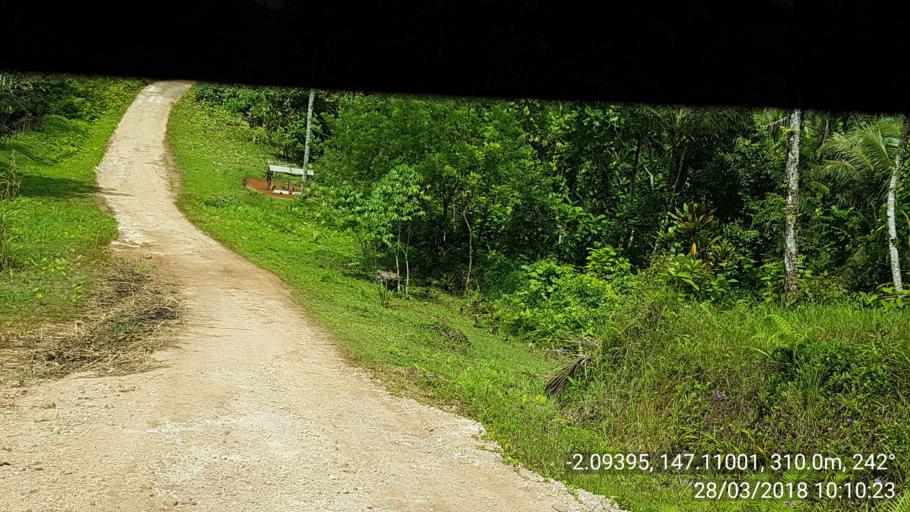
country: PG
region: Manus
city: Lorengau
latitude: -2.0939
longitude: 147.1100
